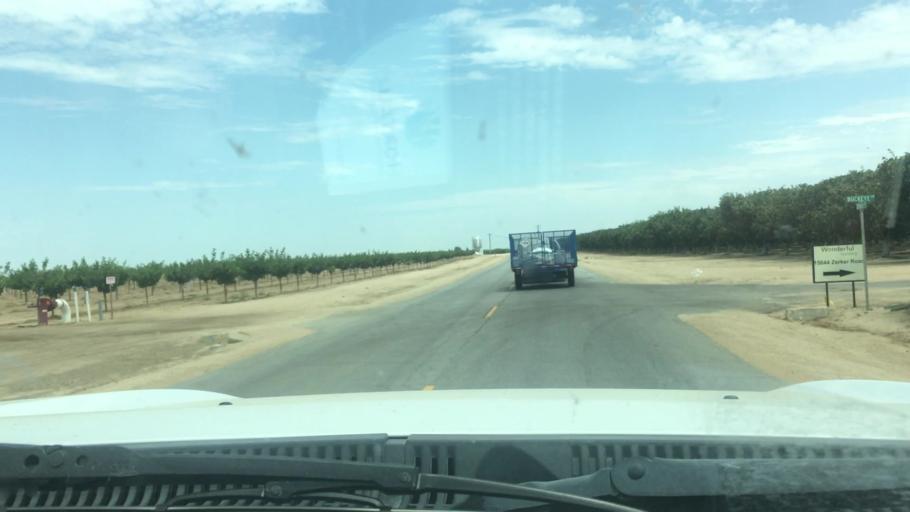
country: US
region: California
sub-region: Kern County
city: McFarland
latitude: 35.5875
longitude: -119.1511
